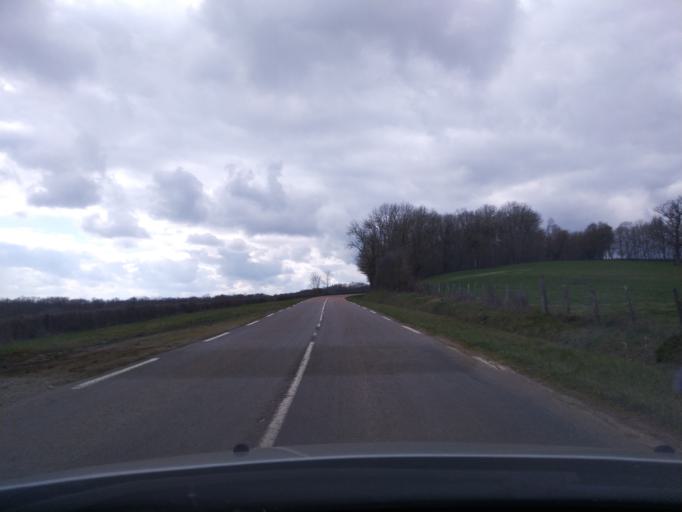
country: FR
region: Bourgogne
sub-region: Departement de l'Yonne
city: Avallon
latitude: 47.5302
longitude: 4.0000
